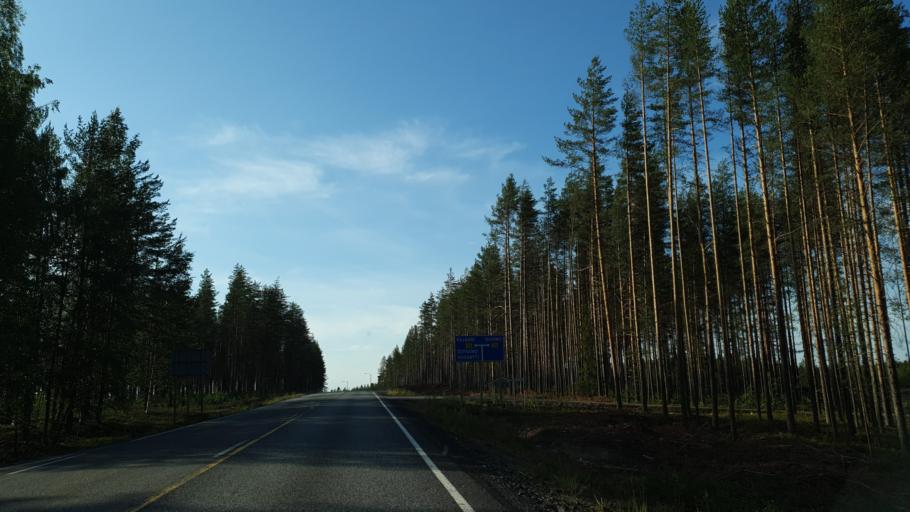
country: FI
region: Kainuu
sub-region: Kehys-Kainuu
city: Kuhmo
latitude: 64.0961
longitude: 29.4770
